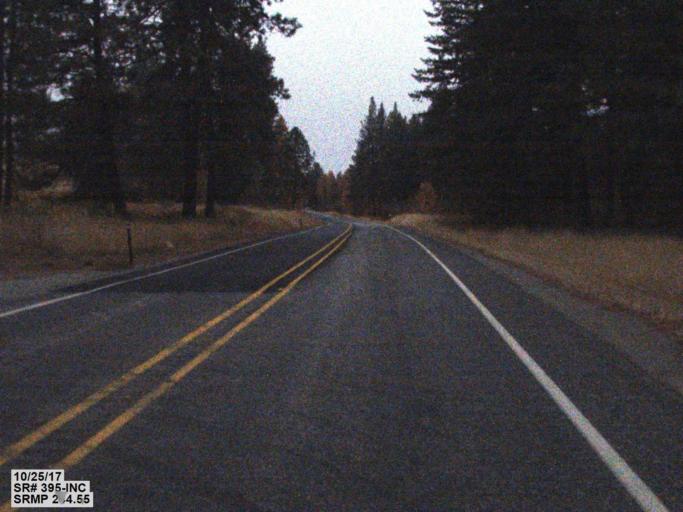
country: US
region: Washington
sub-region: Stevens County
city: Kettle Falls
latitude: 48.6639
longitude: -118.1140
